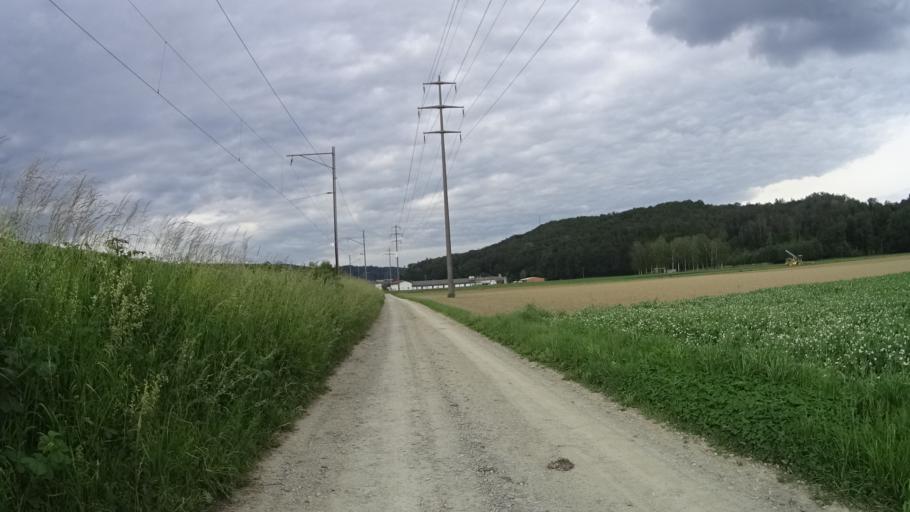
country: CH
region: Aargau
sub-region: Bezirk Zurzach
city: Leibstadt
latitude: 47.6048
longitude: 8.1890
